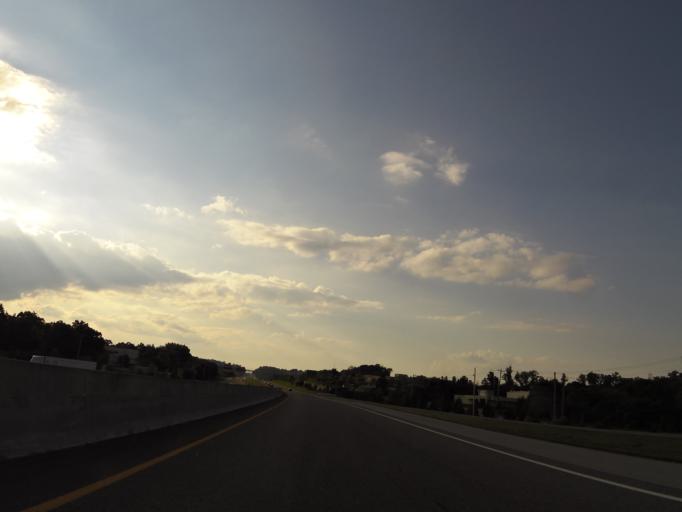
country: US
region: Tennessee
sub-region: Knox County
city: Farragut
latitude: 35.9183
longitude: -84.1255
